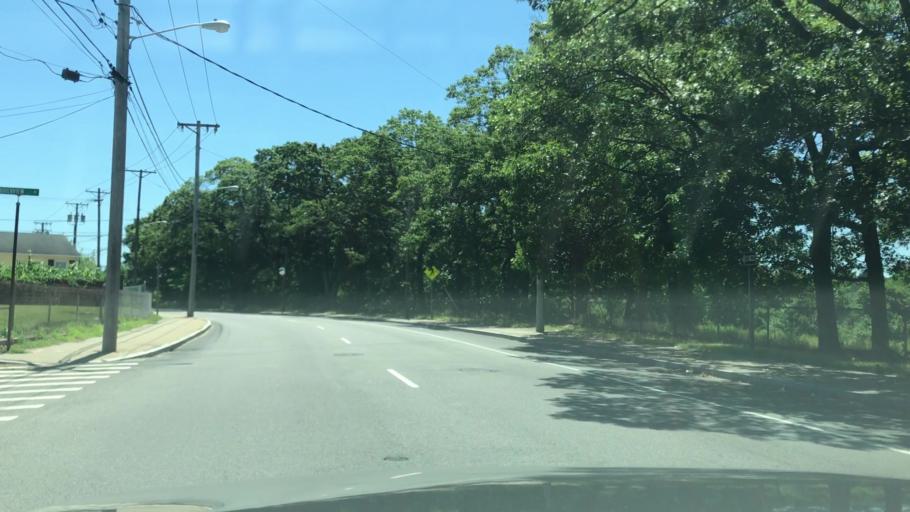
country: US
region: Rhode Island
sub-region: Providence County
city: Pawtucket
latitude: 41.8630
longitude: -71.3752
